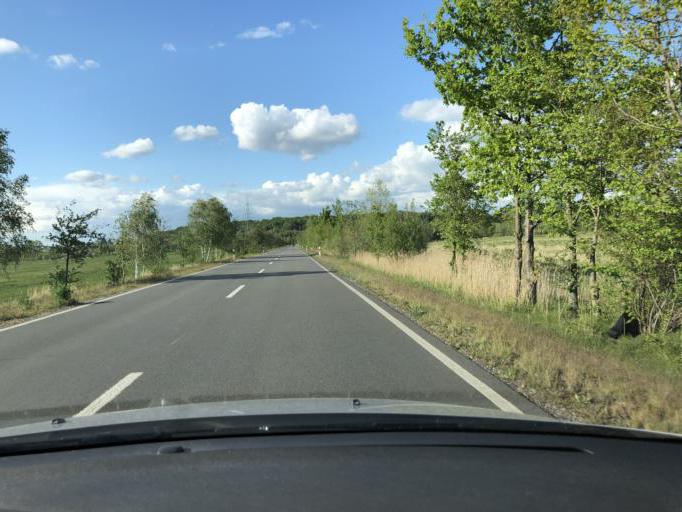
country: DE
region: Saxony
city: Neukieritzsch
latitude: 51.1774
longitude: 12.4193
